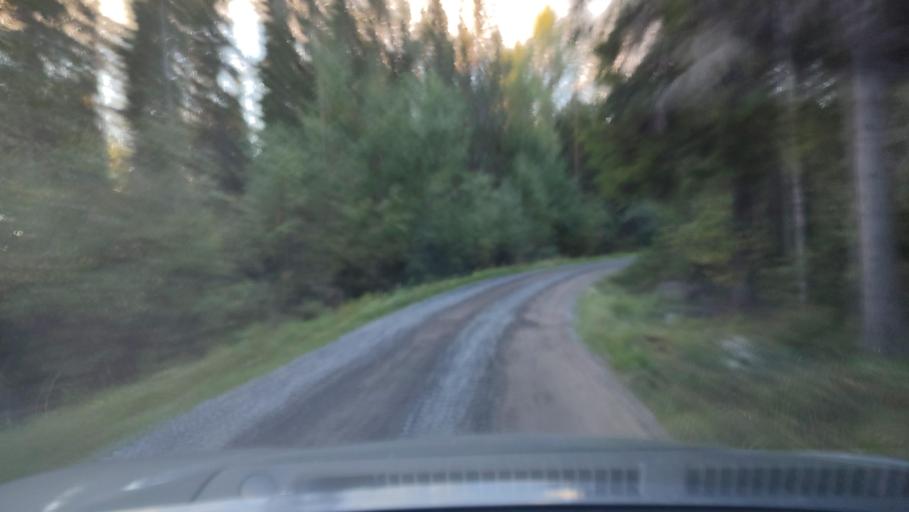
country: FI
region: Southern Ostrobothnia
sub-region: Suupohja
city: Karijoki
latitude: 62.2095
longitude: 21.5716
